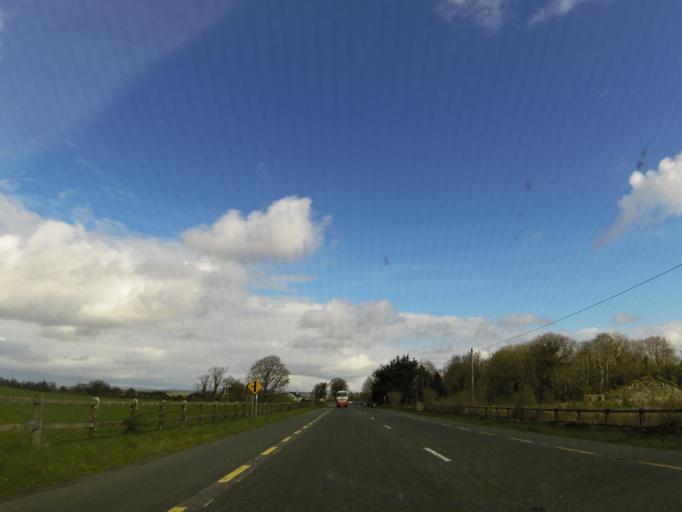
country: IE
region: Connaught
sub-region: Maigh Eo
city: Ballyhaunis
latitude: 53.8433
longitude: -8.8581
